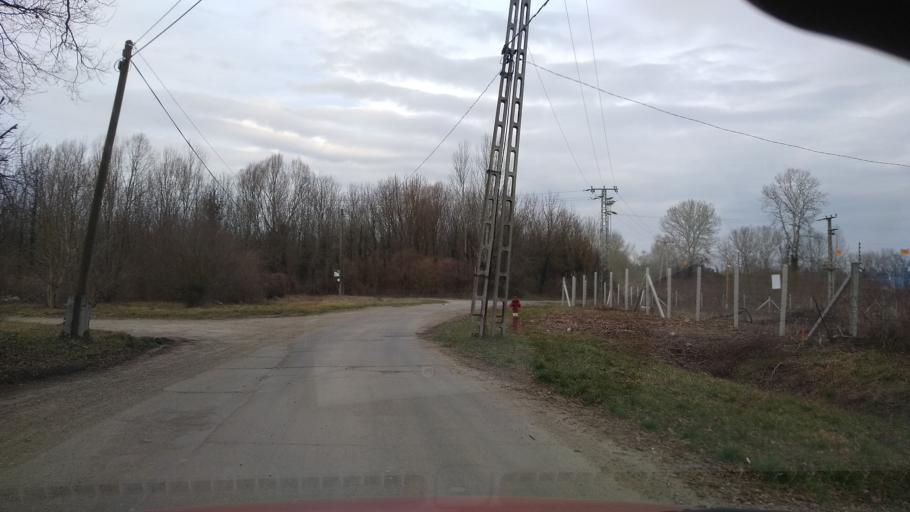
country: HU
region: Somogy
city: Barcs
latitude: 45.9567
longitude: 17.4413
